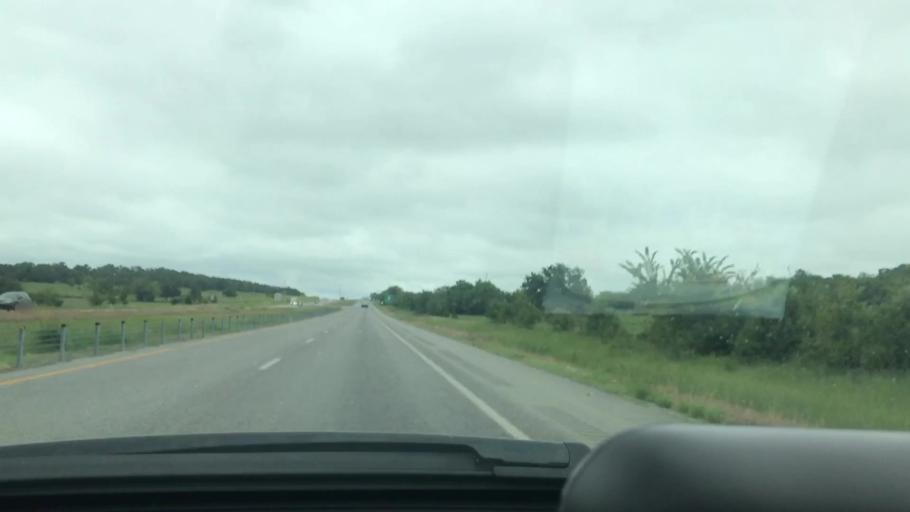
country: US
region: Oklahoma
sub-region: Coal County
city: Coalgate
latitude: 34.6625
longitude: -95.9389
